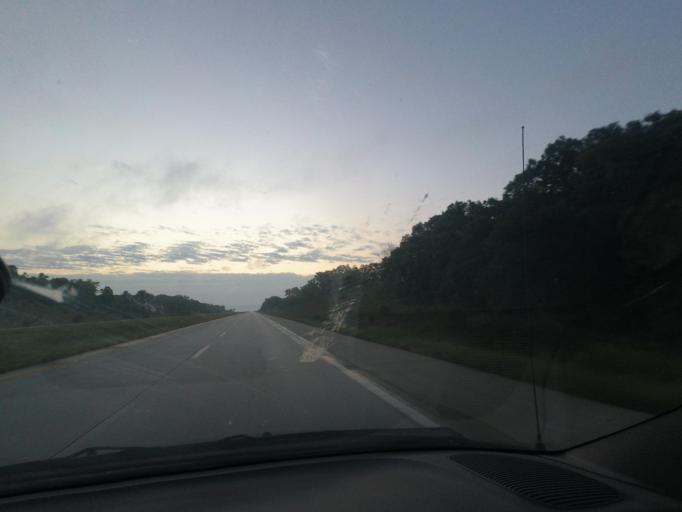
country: US
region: Missouri
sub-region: Linn County
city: Marceline
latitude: 39.7591
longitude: -92.8391
